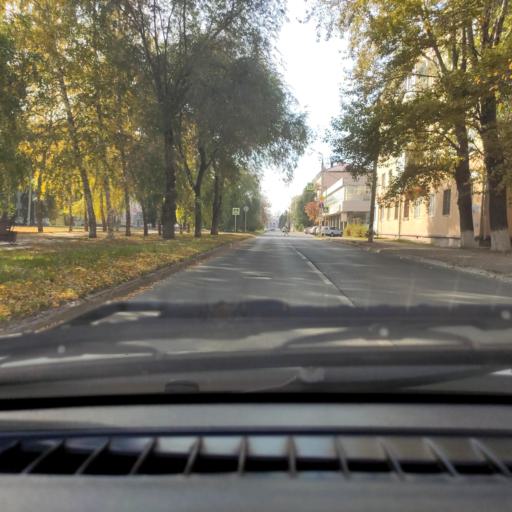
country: RU
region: Samara
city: Tol'yatti
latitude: 53.5157
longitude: 49.4137
